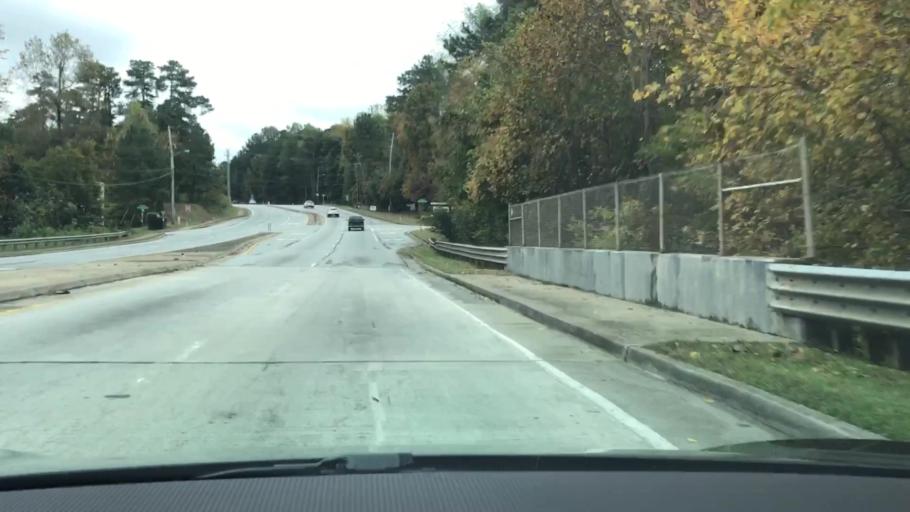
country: US
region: Georgia
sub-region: Gwinnett County
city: Lawrenceville
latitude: 33.9781
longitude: -84.0202
